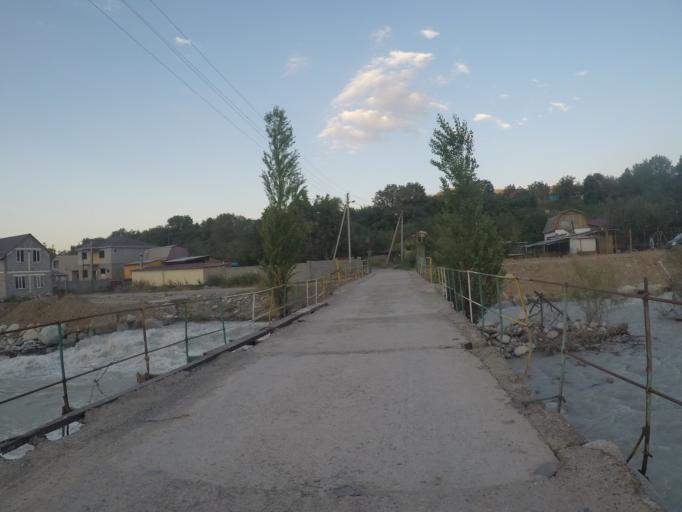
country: KG
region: Chuy
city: Bishkek
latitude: 42.7743
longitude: 74.6417
